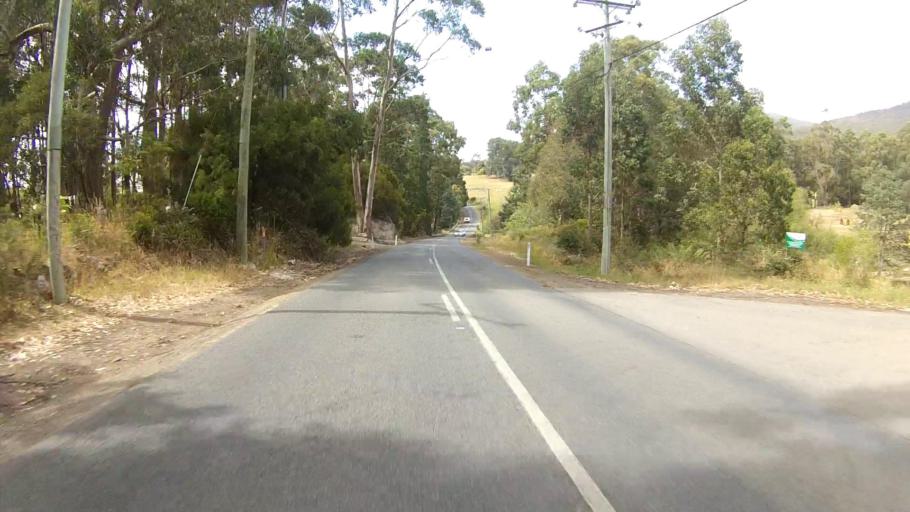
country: AU
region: Tasmania
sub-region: Kingborough
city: Kettering
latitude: -43.1804
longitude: 147.2384
